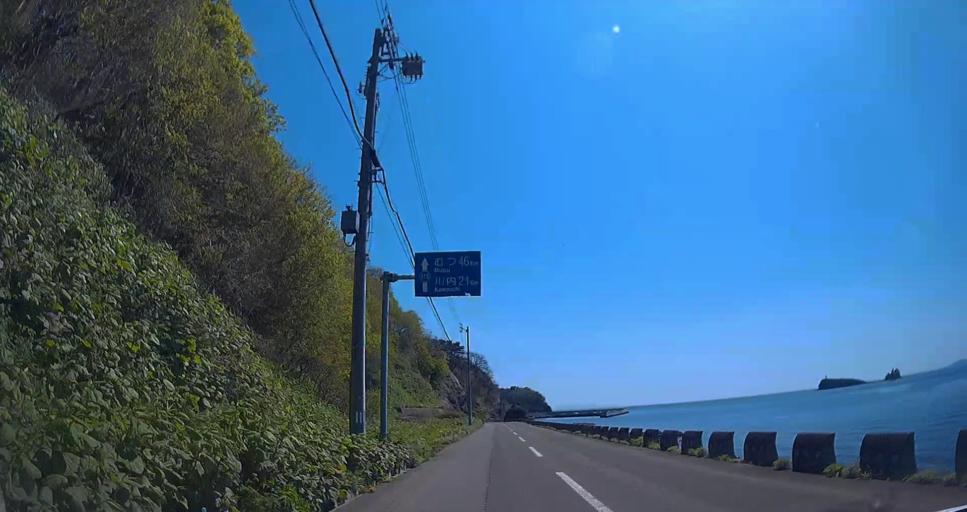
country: JP
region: Aomori
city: Aomori Shi
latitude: 41.1288
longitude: 140.8013
